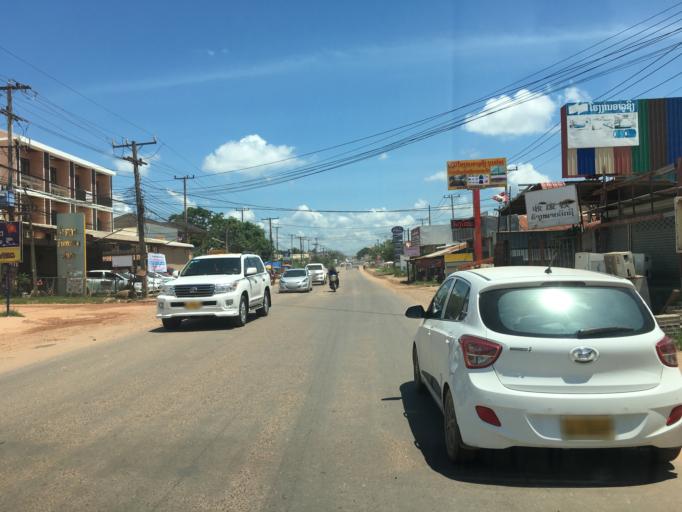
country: TH
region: Nong Khai
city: Si Chiang Mai
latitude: 18.0065
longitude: 102.5449
